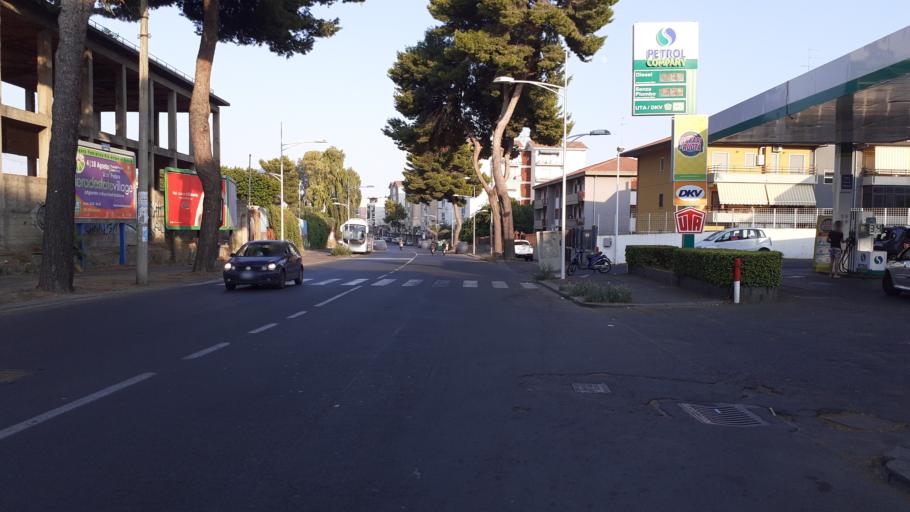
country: IT
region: Sicily
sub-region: Catania
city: Catania
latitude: 37.5030
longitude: 15.0583
